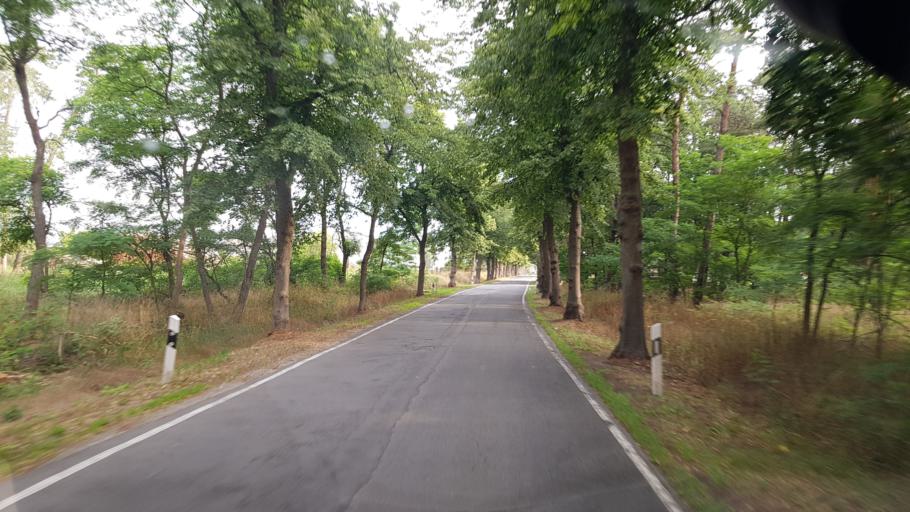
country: DE
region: Brandenburg
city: Dahme
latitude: 51.9400
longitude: 13.3959
